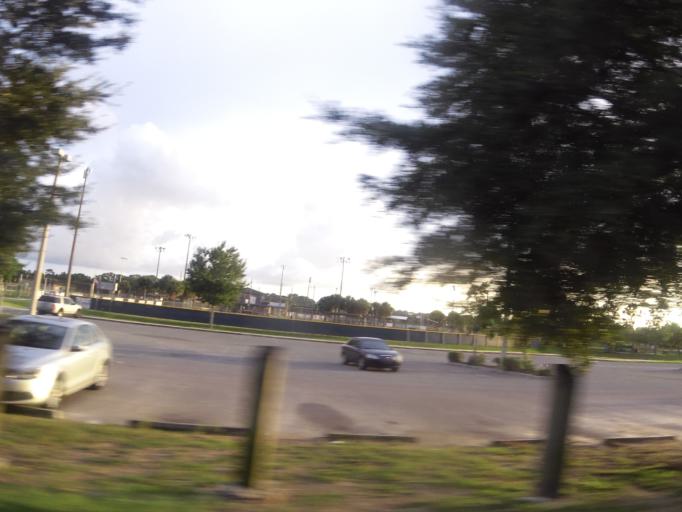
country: US
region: Florida
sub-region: Duval County
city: Atlantic Beach
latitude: 30.3665
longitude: -81.5043
